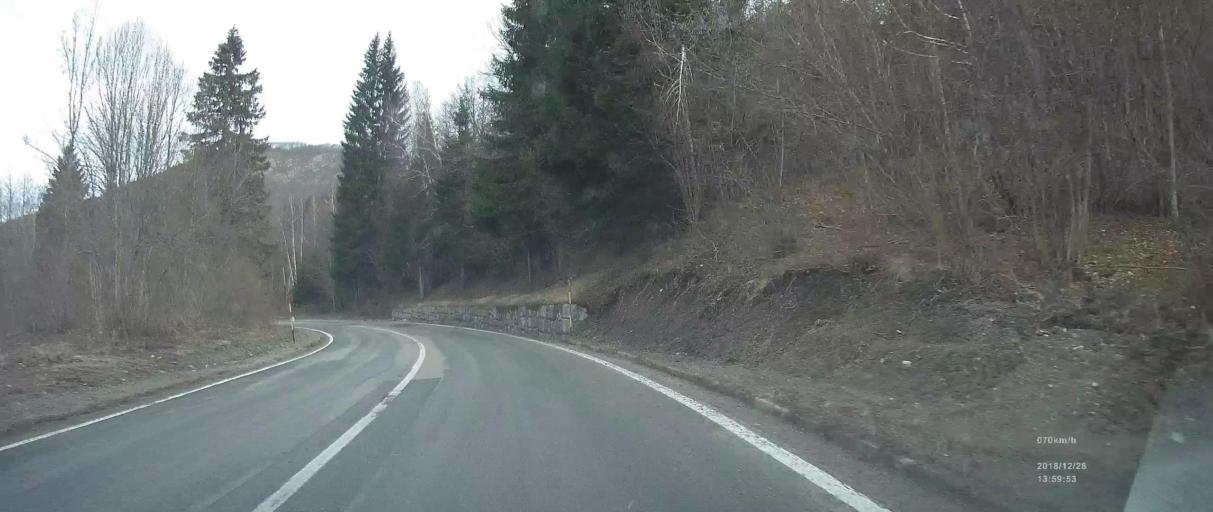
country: SI
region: Kostel
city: Kostel
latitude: 45.4063
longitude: 14.9132
